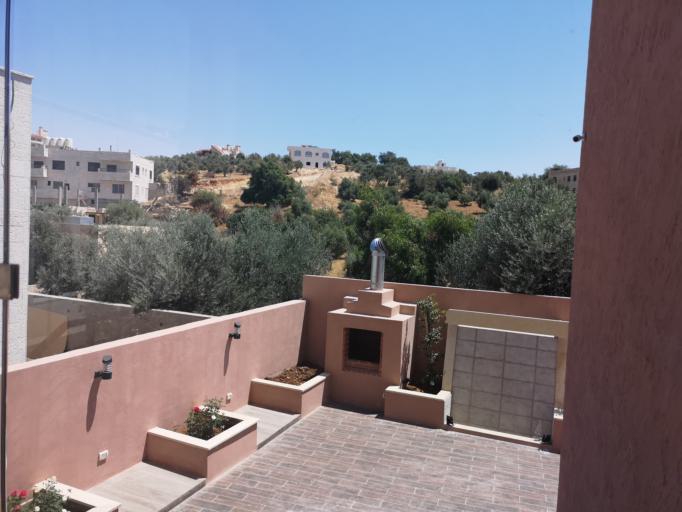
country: JO
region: Amman
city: Wadi as Sir
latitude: 31.9683
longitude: 35.7741
